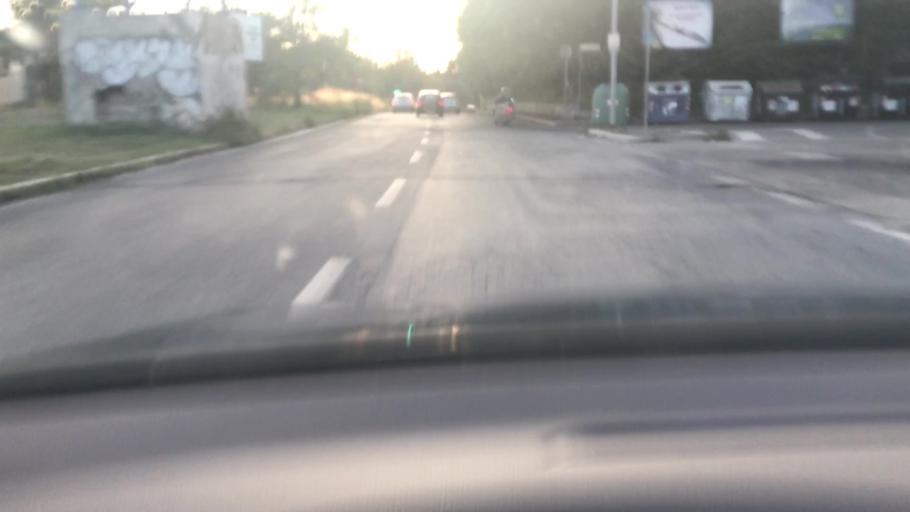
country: IT
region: Latium
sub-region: Citta metropolitana di Roma Capitale
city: Rome
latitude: 41.9319
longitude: 12.5603
